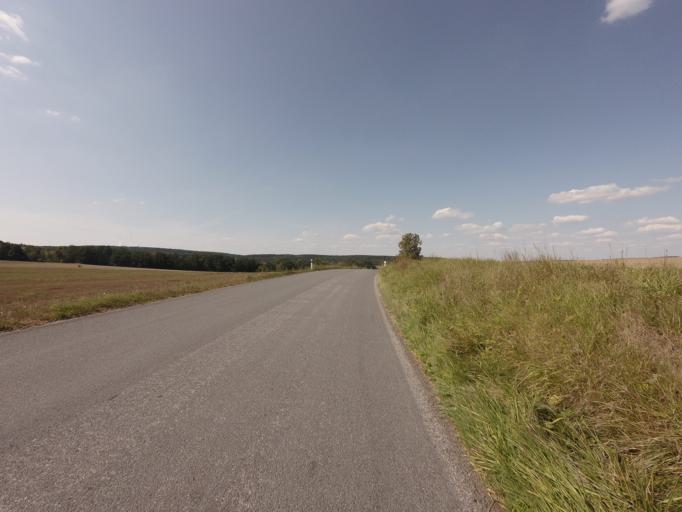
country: CZ
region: Jihocesky
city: Tyn nad Vltavou
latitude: 49.1450
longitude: 14.4458
